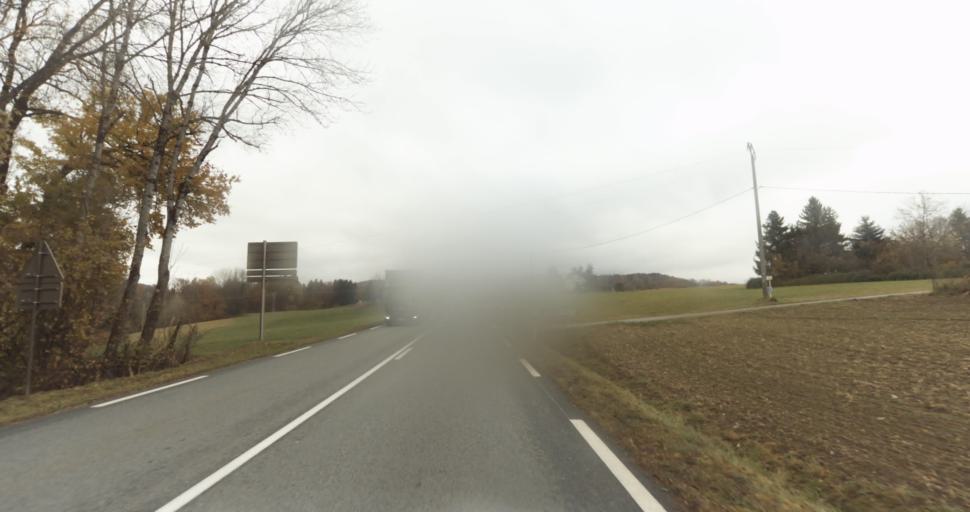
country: FR
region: Rhone-Alpes
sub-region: Departement de la Haute-Savoie
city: Groisy
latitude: 46.0072
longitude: 6.1994
